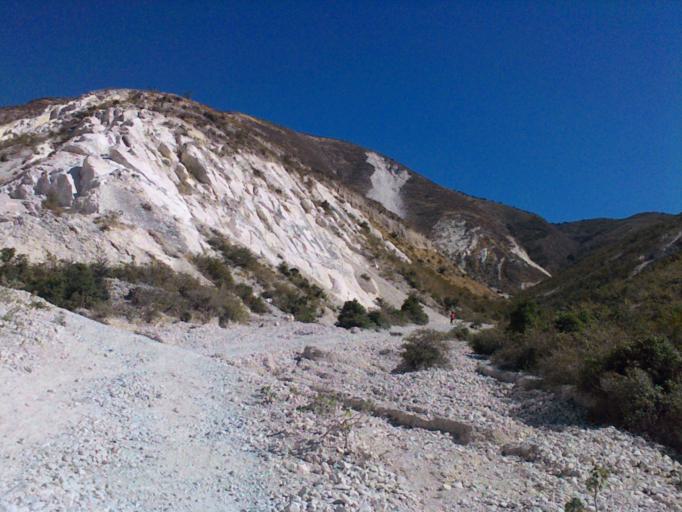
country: HT
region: Ouest
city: Croix des Bouquets
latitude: 18.6799
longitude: -72.2332
